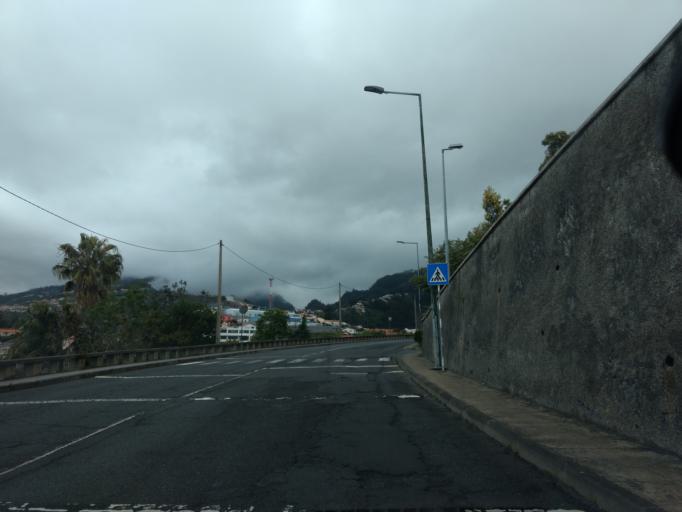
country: PT
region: Madeira
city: Camara de Lobos
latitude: 32.6630
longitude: -16.9487
